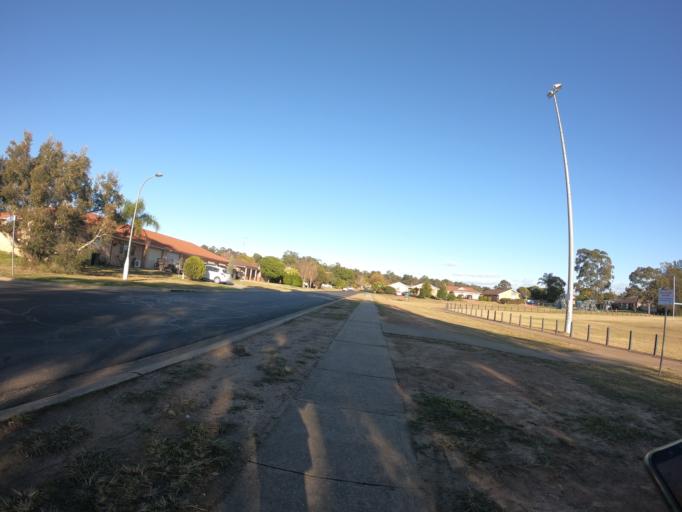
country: AU
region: New South Wales
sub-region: Hawkesbury
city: South Windsor
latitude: -33.6404
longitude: 150.8002
